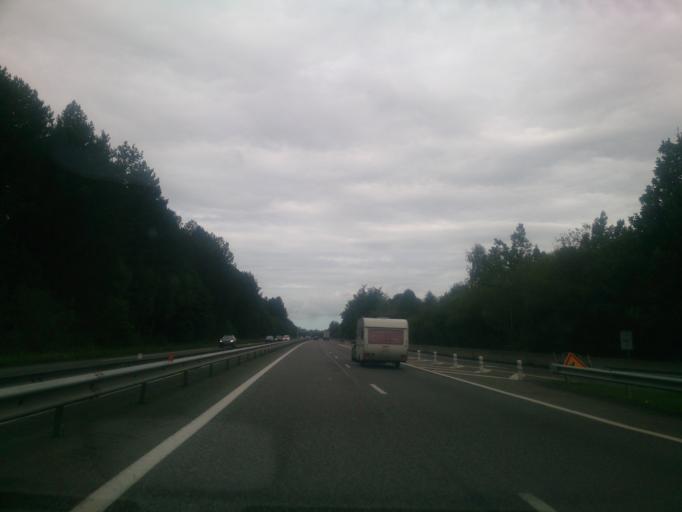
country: FR
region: Midi-Pyrenees
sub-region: Departement des Hautes-Pyrenees
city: Lannemezan
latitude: 43.1050
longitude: 0.4705
